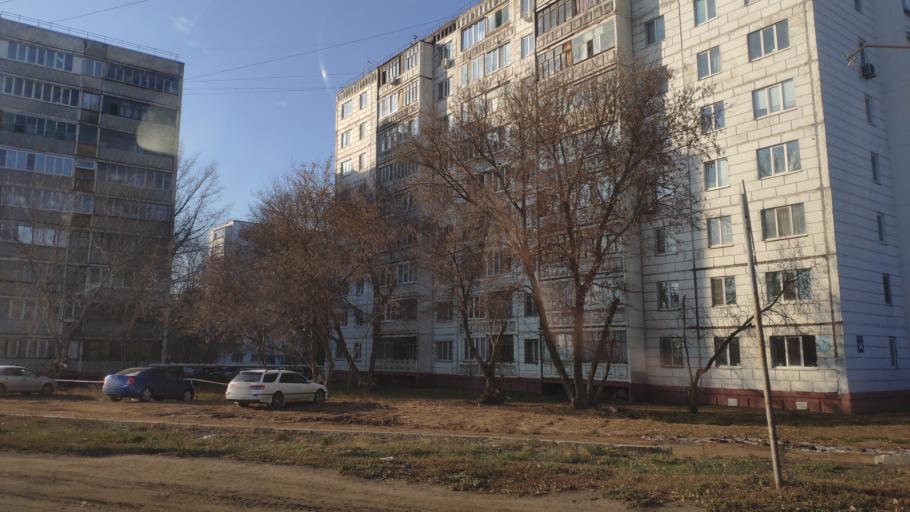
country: RU
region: Orenburg
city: Prigorodnyy
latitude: 51.7771
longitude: 55.1914
